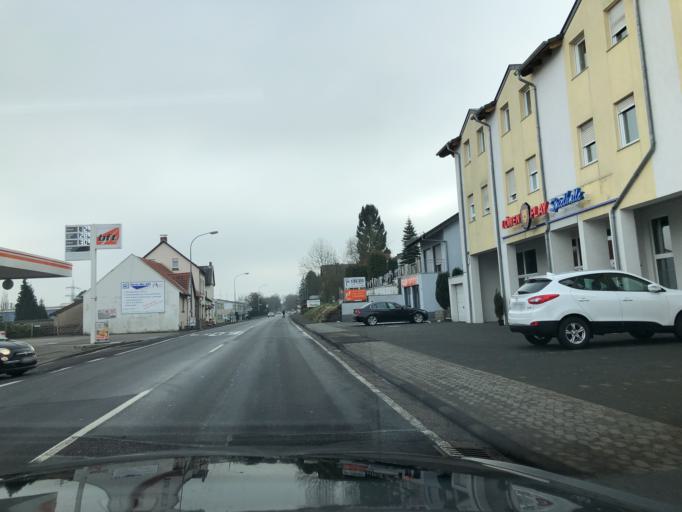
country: DE
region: Rheinland-Pfalz
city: Erpel
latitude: 50.5710
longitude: 7.2377
